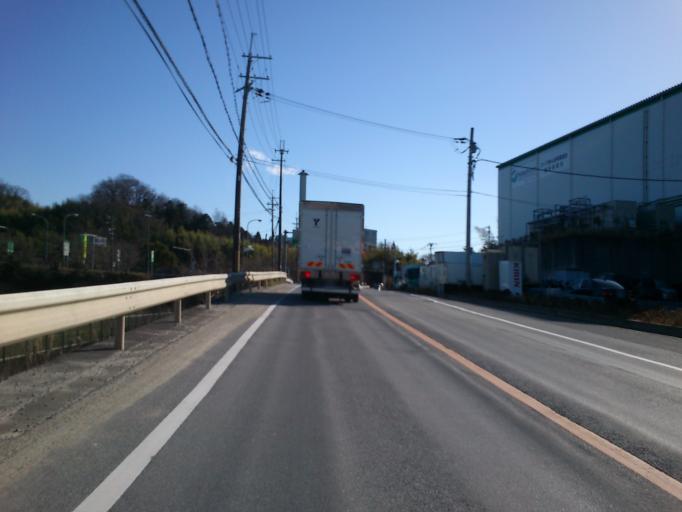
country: JP
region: Kyoto
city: Tanabe
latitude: 34.8103
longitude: 135.7527
